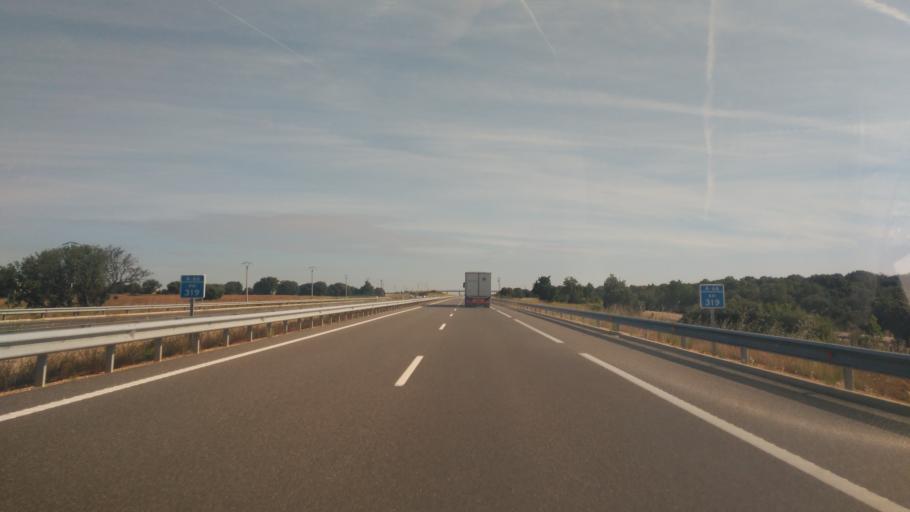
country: ES
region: Castille and Leon
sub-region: Provincia de Salamanca
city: Topas
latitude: 41.1506
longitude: -5.6959
